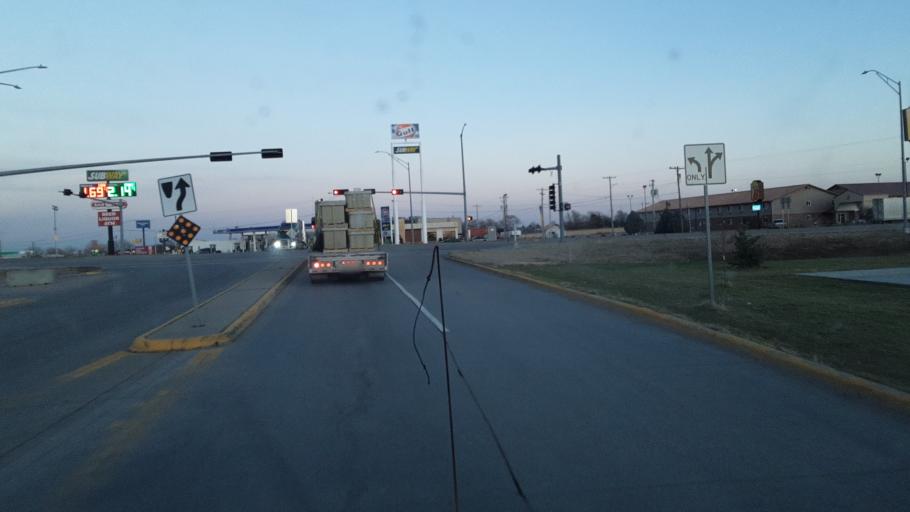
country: US
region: Nebraska
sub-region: Keith County
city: Ogallala
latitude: 41.1123
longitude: -101.7166
